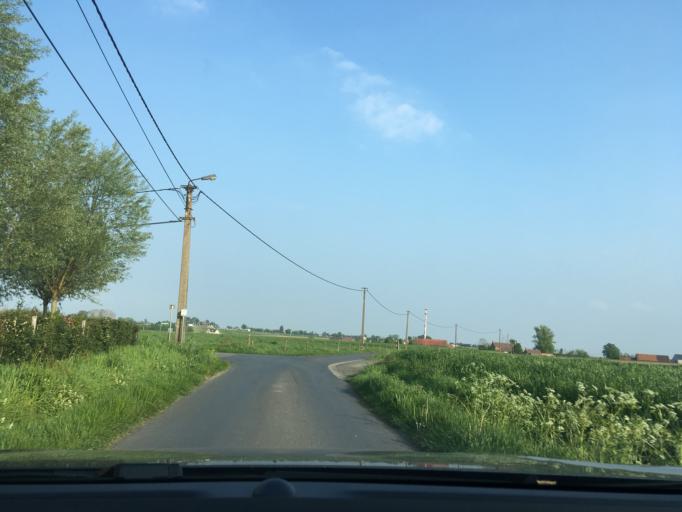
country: BE
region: Flanders
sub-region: Provincie West-Vlaanderen
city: Lichtervelde
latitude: 51.0129
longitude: 3.1578
